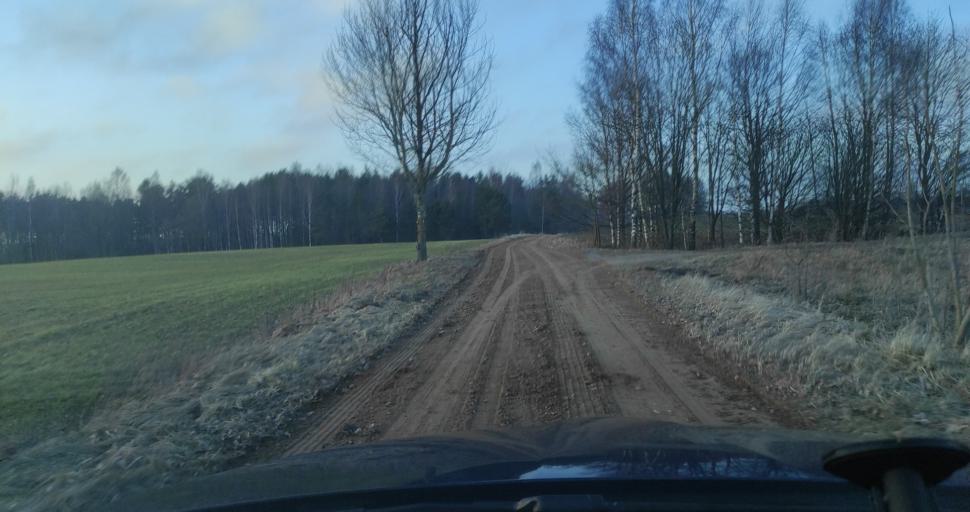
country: LV
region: Aizpute
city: Aizpute
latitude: 56.8022
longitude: 21.8041
